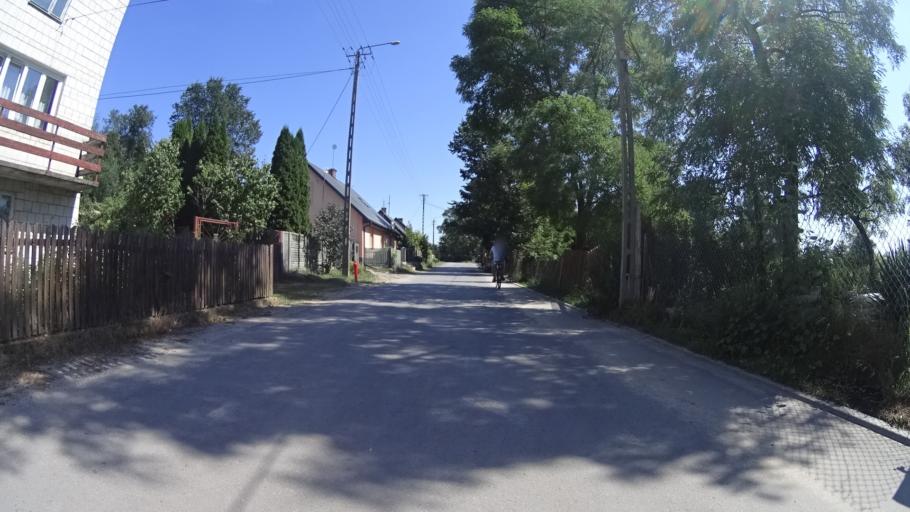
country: PL
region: Masovian Voivodeship
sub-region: Powiat bialobrzeski
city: Wysmierzyce
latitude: 51.6631
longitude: 20.8671
